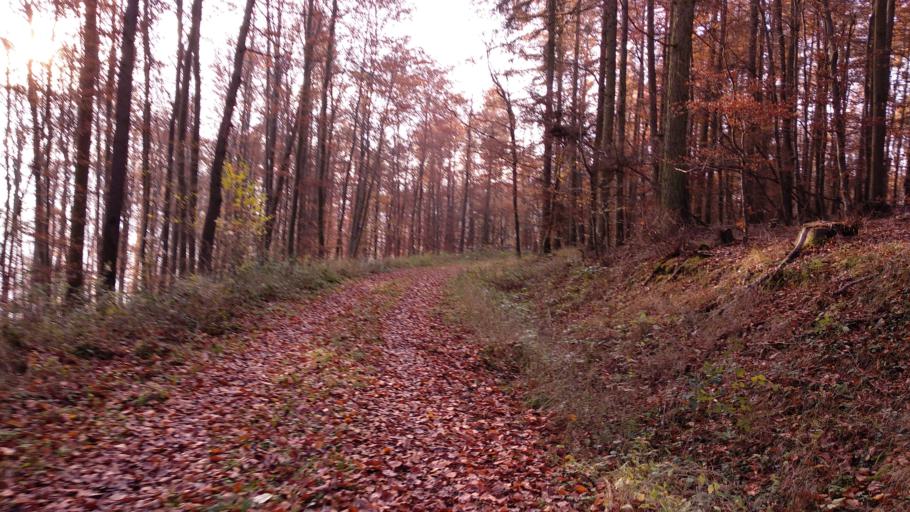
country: DE
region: North Rhine-Westphalia
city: Beverungen
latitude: 51.6594
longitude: 9.3388
